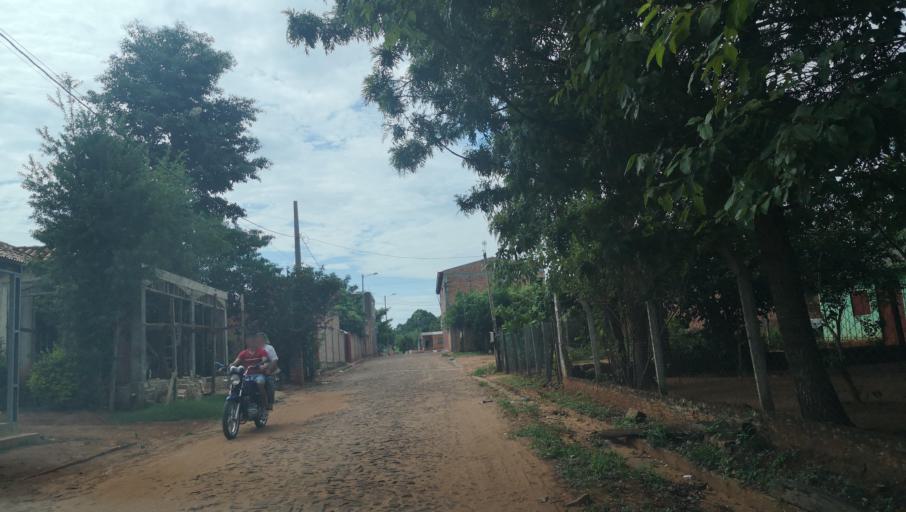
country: PY
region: San Pedro
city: Capiibary
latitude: -24.7215
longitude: -56.0171
